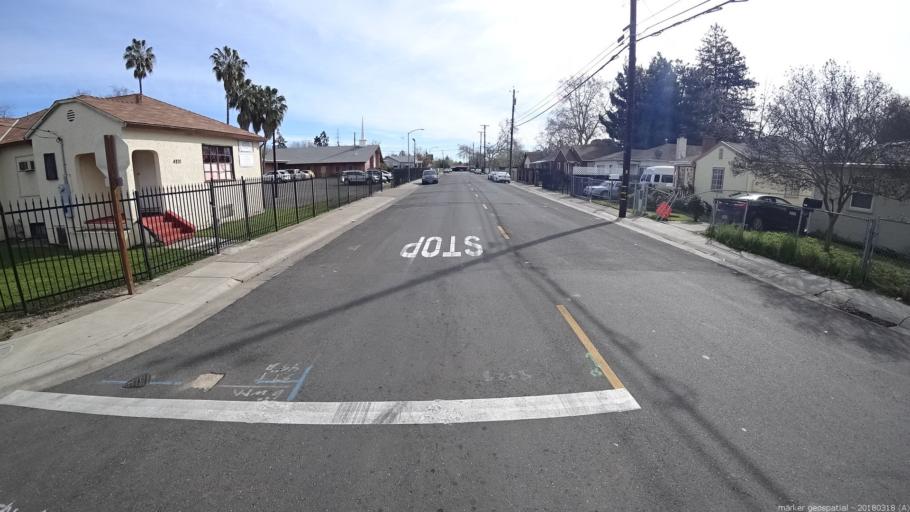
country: US
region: California
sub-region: Sacramento County
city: Parkway
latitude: 38.5337
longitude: -121.4499
